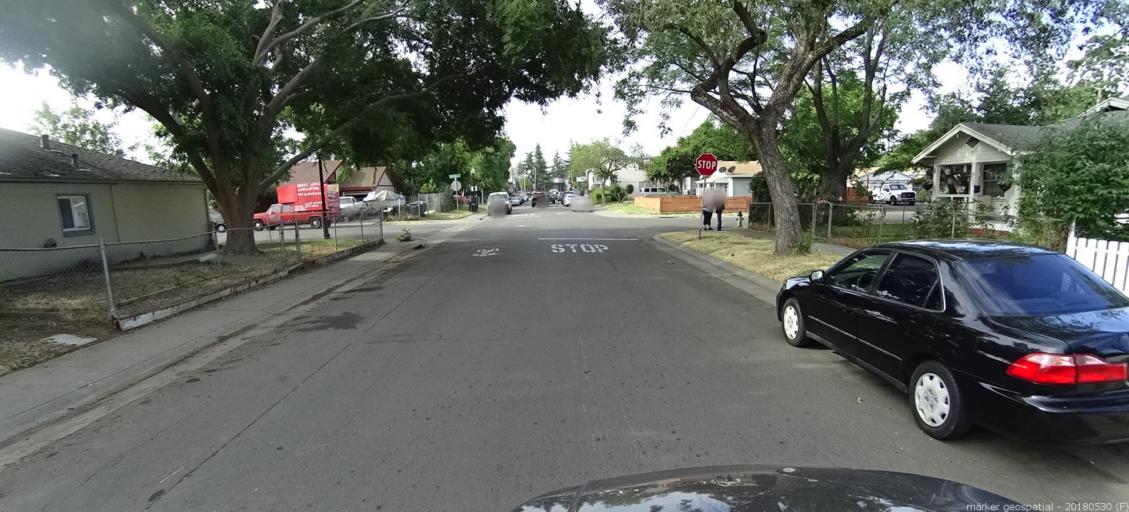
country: US
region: California
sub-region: Sacramento County
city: Sacramento
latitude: 38.6078
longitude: -121.4486
